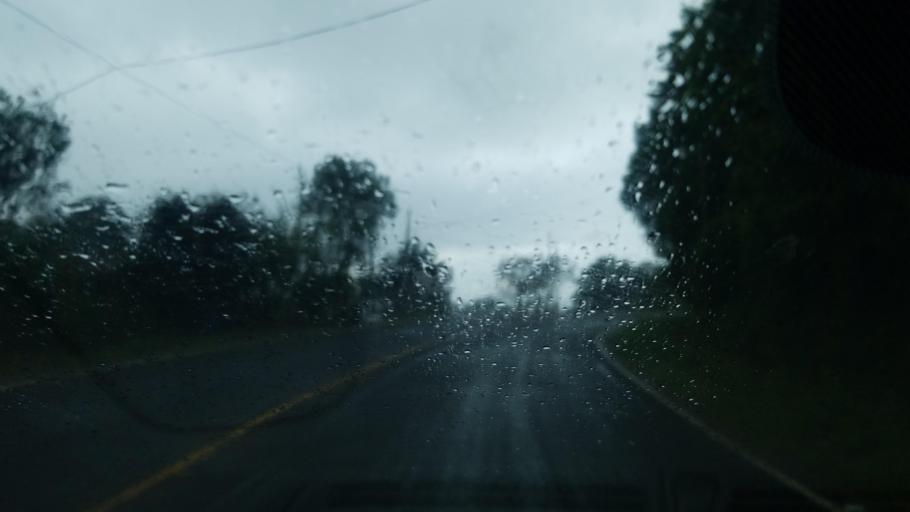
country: HN
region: Ocotepeque
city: La Labor
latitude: 14.4681
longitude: -89.0890
